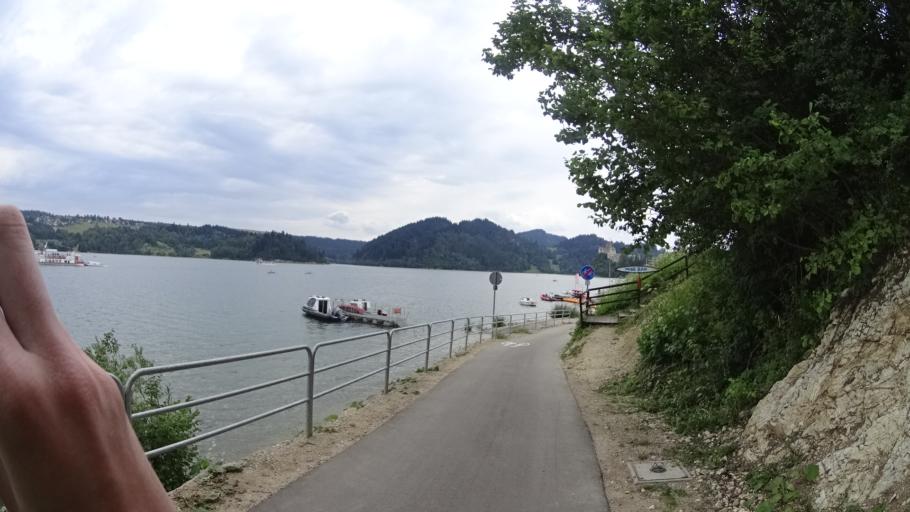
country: PL
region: Lesser Poland Voivodeship
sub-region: Powiat nowotarski
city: Niedzica
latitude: 49.4261
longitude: 20.3098
